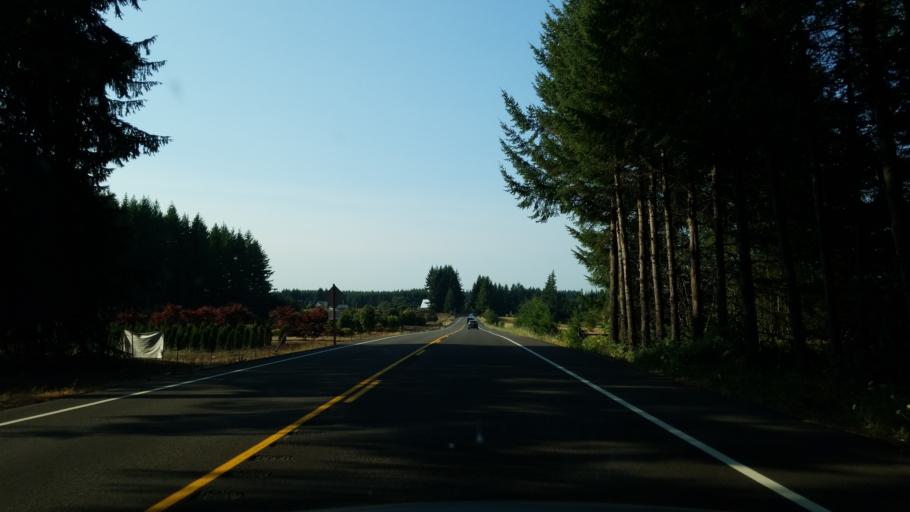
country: US
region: Oregon
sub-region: Clackamas County
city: Estacada
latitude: 45.2434
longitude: -122.3280
